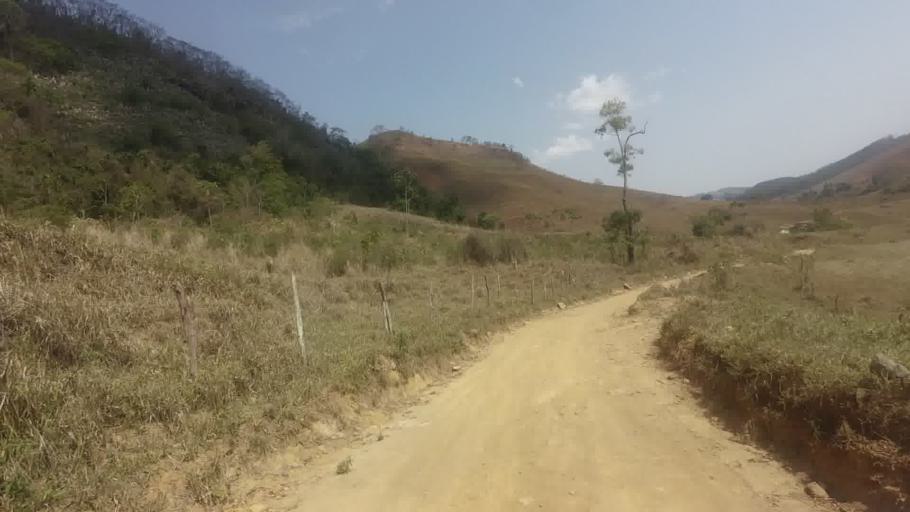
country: BR
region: Espirito Santo
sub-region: Sao Jose Do Calcado
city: Sao Jose do Calcado
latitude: -21.0080
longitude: -41.5086
